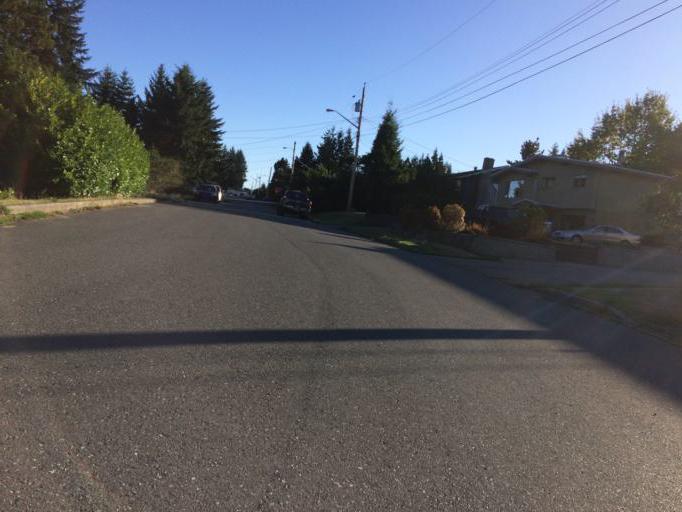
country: CA
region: British Columbia
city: Campbell River
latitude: 49.9883
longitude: -125.2308
